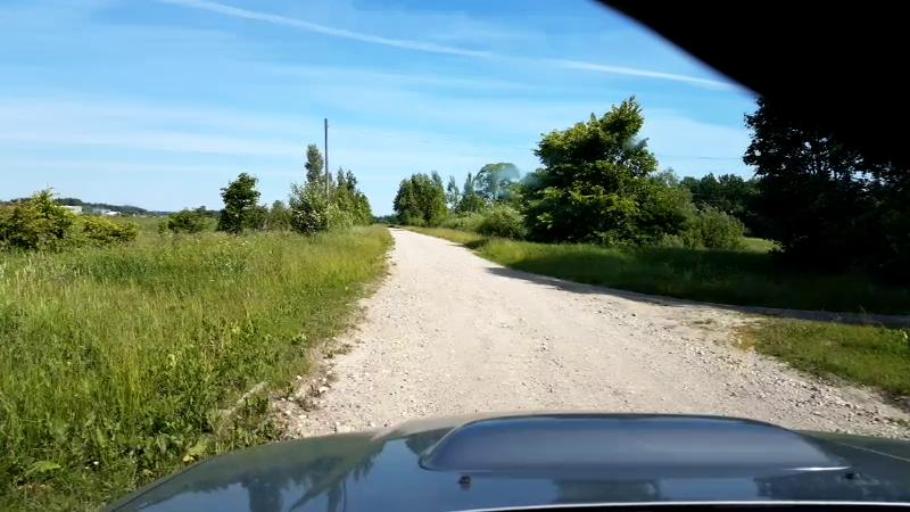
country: EE
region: Paernumaa
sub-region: Sauga vald
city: Sauga
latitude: 58.4747
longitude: 24.5340
